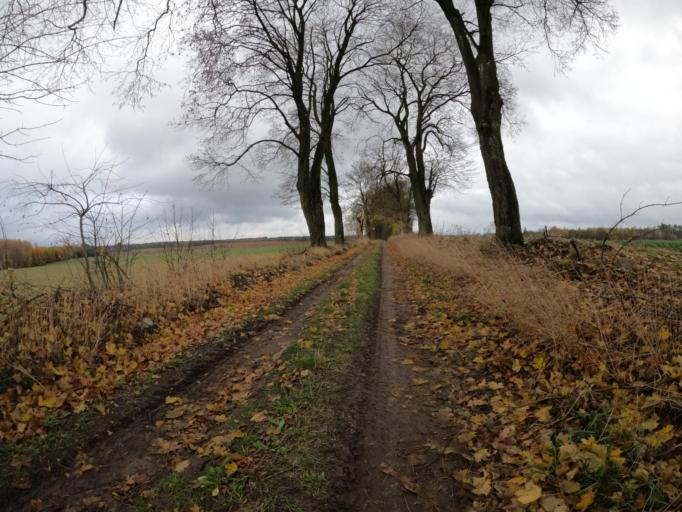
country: PL
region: West Pomeranian Voivodeship
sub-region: Powiat walecki
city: Tuczno
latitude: 53.2398
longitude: 16.2322
